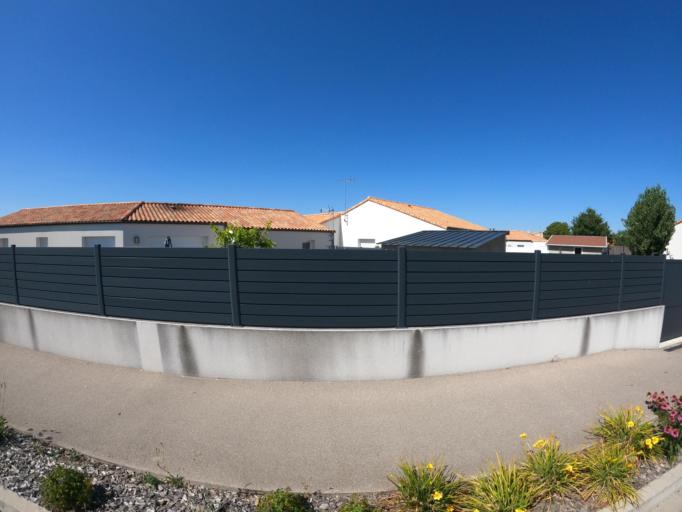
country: FR
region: Pays de la Loire
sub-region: Departement de la Vendee
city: Les Landes-Genusson
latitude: 46.9615
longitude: -1.1258
